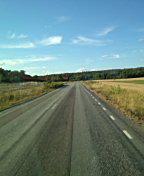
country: SE
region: Uppsala
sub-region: Habo Kommun
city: Balsta
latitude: 59.6613
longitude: 17.5554
